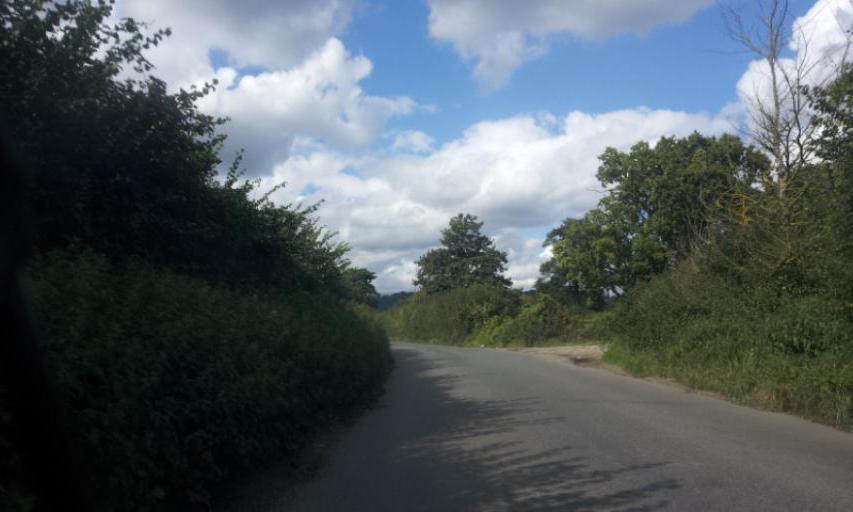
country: GB
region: England
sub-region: Kent
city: West Malling
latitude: 51.3145
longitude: 0.4143
